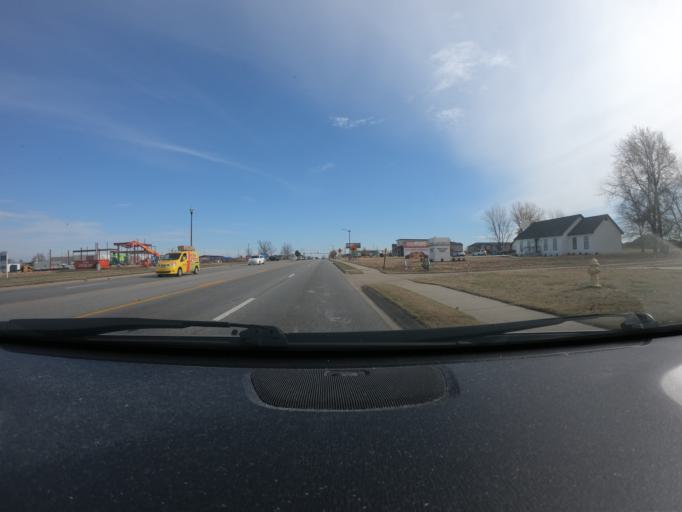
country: US
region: Arkansas
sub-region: Benton County
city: Bentonville
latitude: 36.3357
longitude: -94.2266
